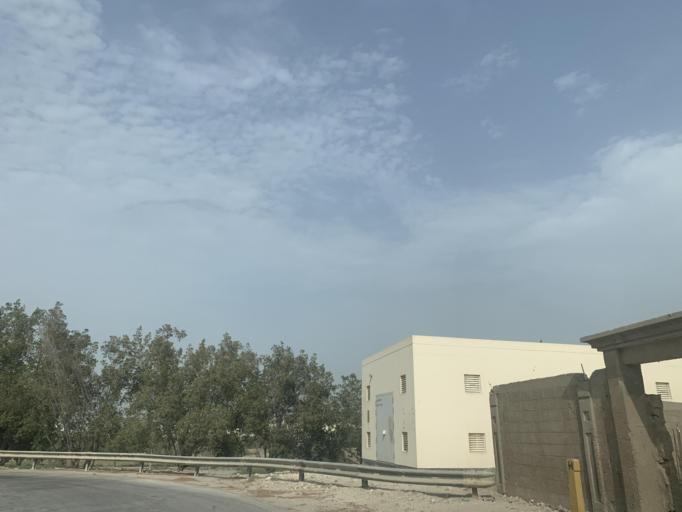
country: BH
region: Northern
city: Madinat `Isa
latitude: 26.1888
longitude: 50.4879
